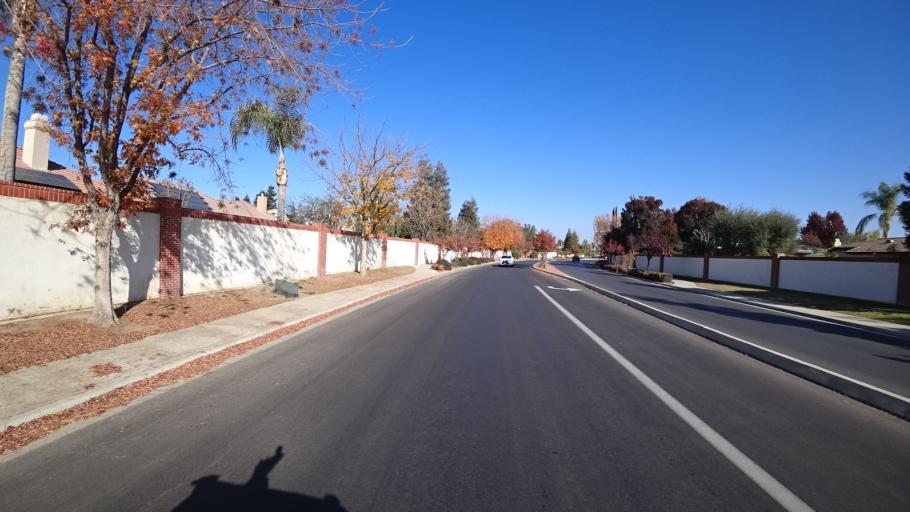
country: US
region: California
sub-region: Kern County
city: Rosedale
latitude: 35.3305
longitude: -119.1303
